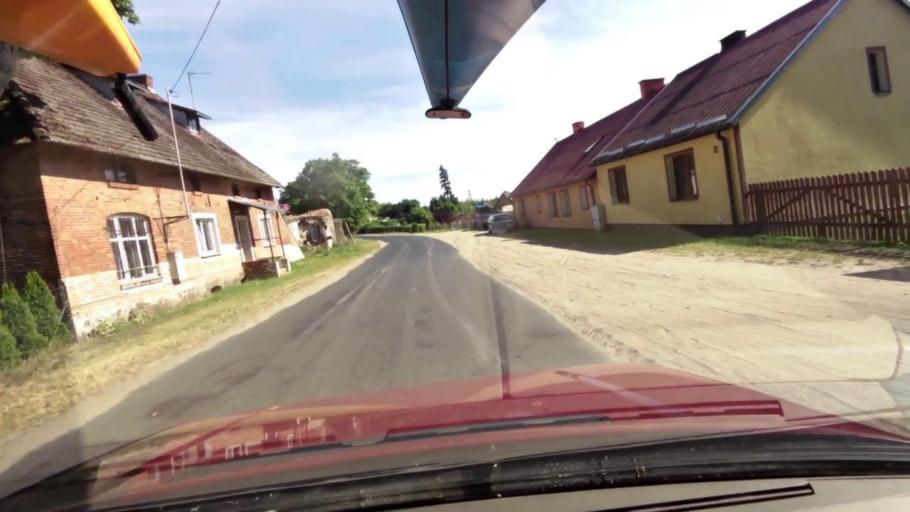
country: PL
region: Pomeranian Voivodeship
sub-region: Powiat bytowski
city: Miastko
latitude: 54.1203
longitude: 16.9458
